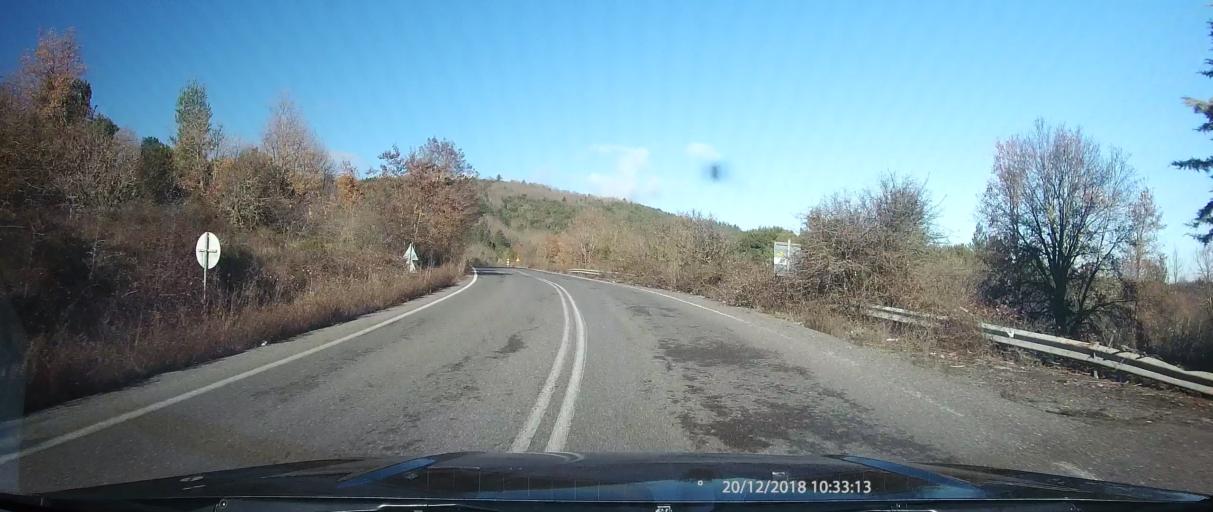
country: GR
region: Peloponnese
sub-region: Nomos Lakonias
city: Kariai
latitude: 37.3360
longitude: 22.4177
